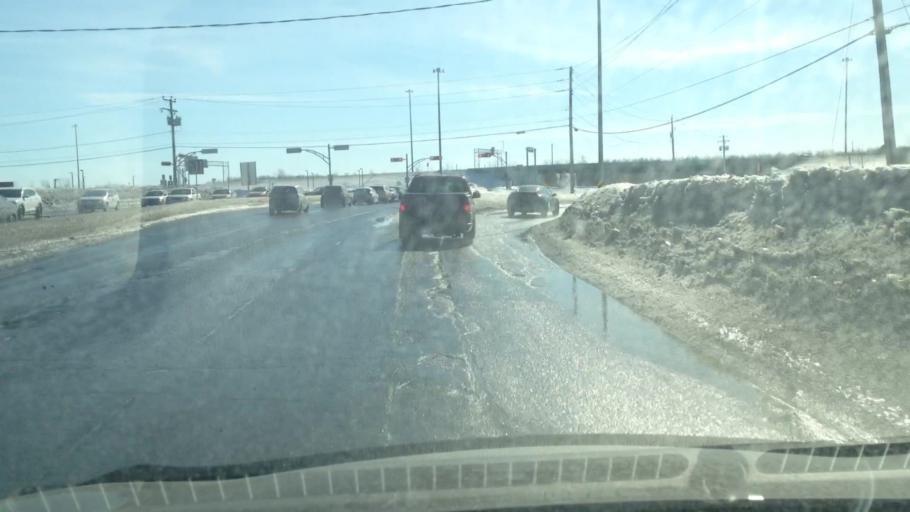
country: CA
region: Quebec
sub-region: Laurentides
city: Saint-Jerome
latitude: 45.7475
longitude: -74.0006
